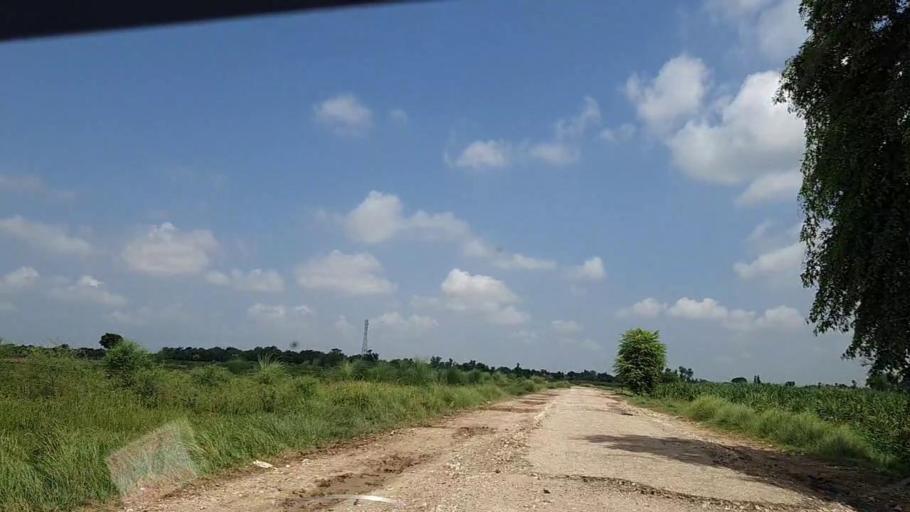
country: PK
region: Sindh
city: Tharu Shah
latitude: 26.9056
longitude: 68.0378
